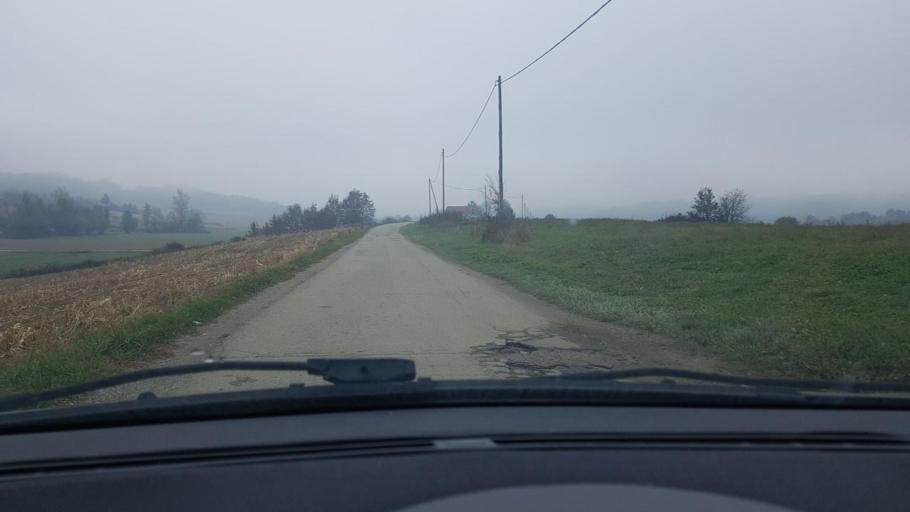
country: HR
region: Krapinsko-Zagorska
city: Zlatar
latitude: 46.1108
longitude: 16.1780
